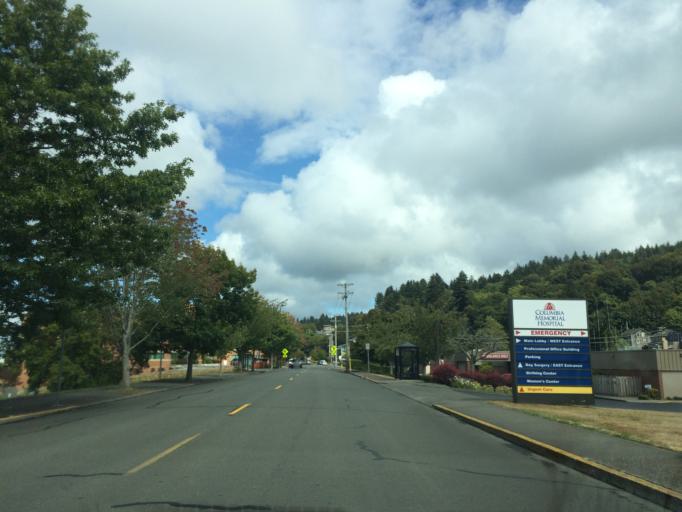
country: US
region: Oregon
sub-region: Clatsop County
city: Astoria
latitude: 46.1884
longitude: -123.8201
